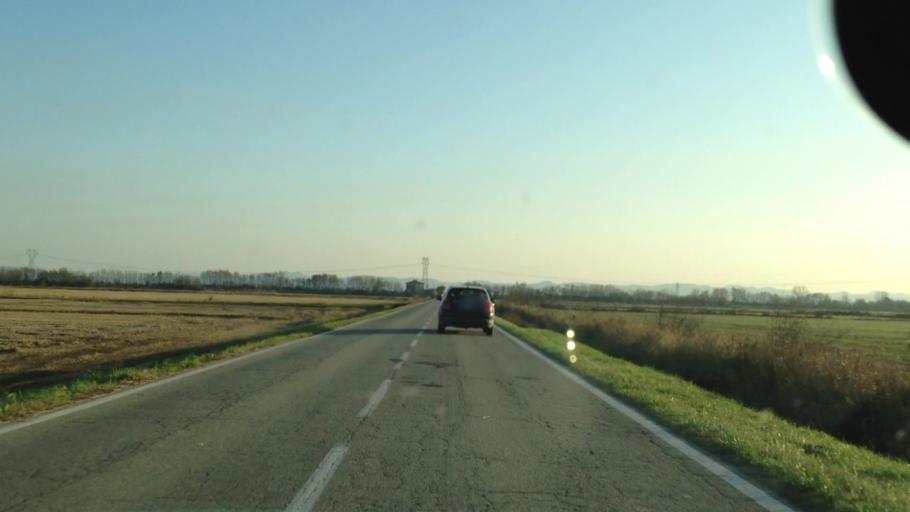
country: IT
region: Piedmont
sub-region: Provincia di Vercelli
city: Lamporo
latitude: 45.2517
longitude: 8.0879
